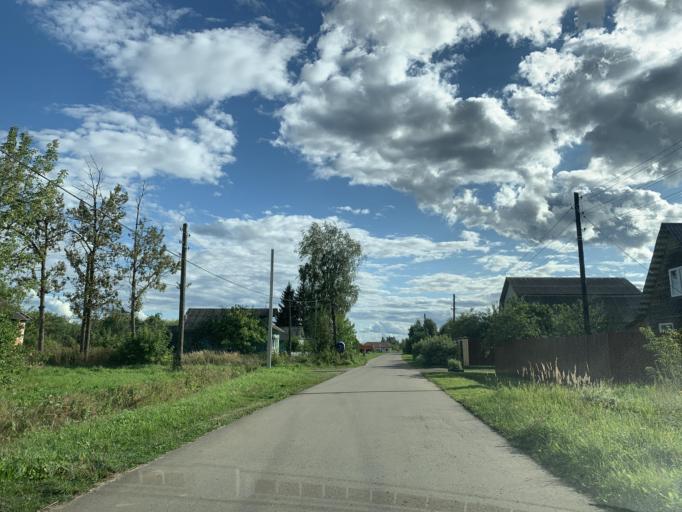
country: RU
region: Jaroslavl
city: Tunoshna
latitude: 57.6616
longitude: 40.0714
